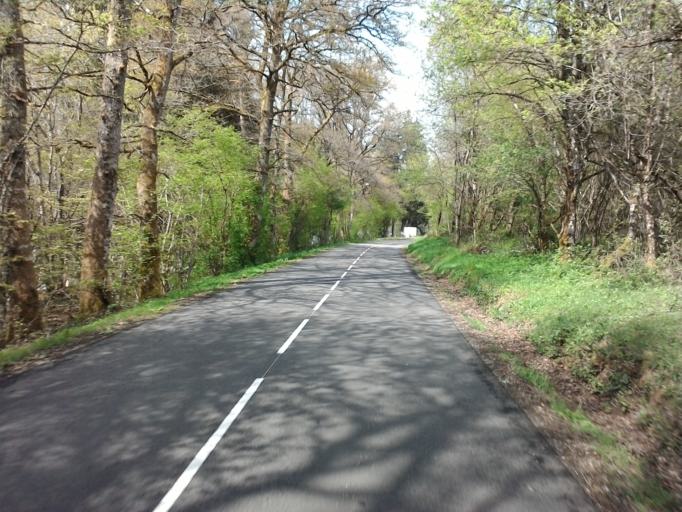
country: FR
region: Bourgogne
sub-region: Departement de la Cote-d'Or
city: Saulieu
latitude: 47.1884
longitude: 4.0743
